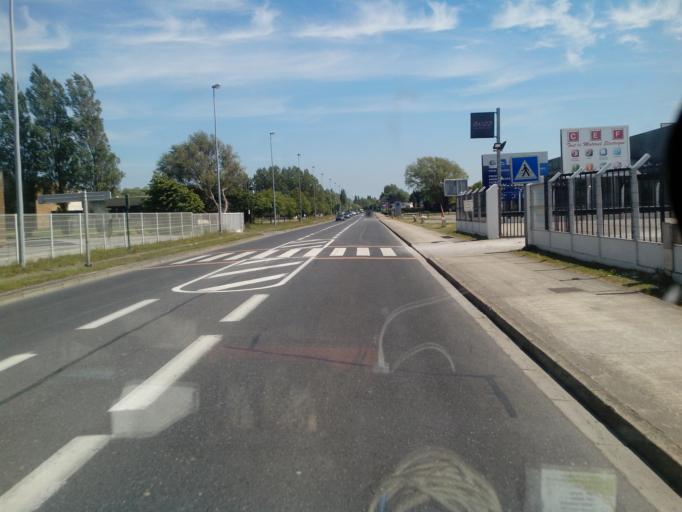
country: FR
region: Nord-Pas-de-Calais
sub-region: Departement du Pas-de-Calais
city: Saint-Leonard
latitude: 50.6916
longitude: 1.6138
